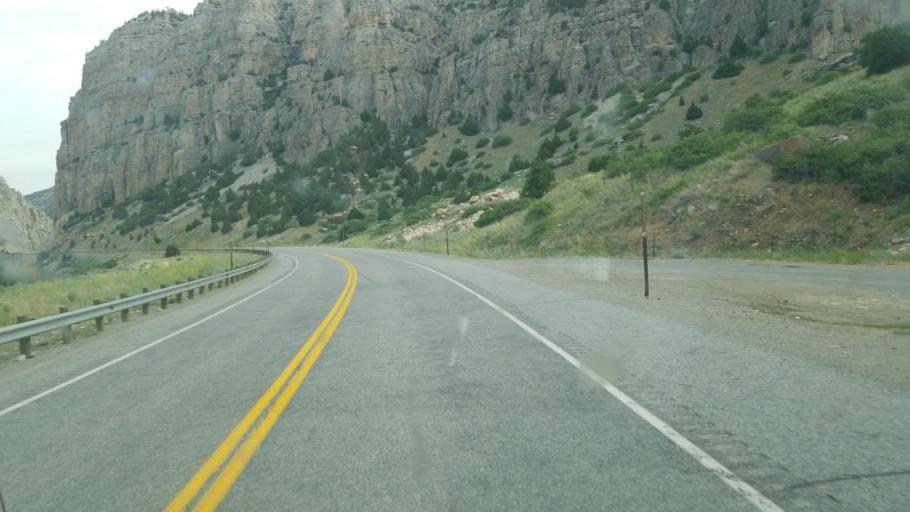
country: US
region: Wyoming
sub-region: Hot Springs County
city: Thermopolis
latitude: 43.5254
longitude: -108.1749
